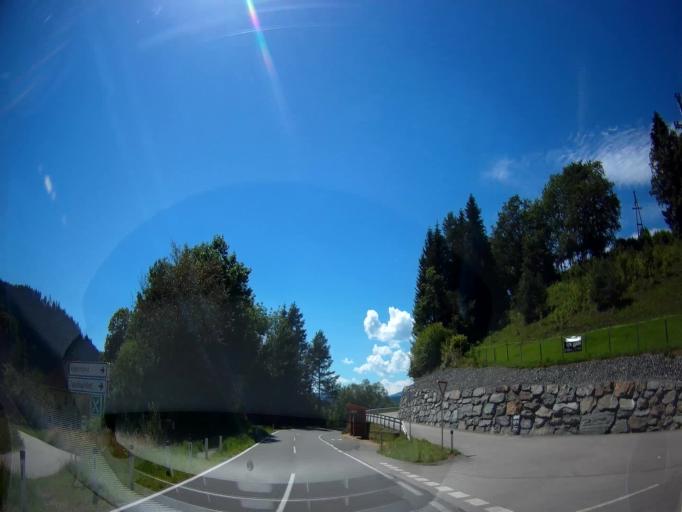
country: AT
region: Carinthia
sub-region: Politischer Bezirk Sankt Veit an der Glan
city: Glodnitz
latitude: 46.8509
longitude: 14.1667
